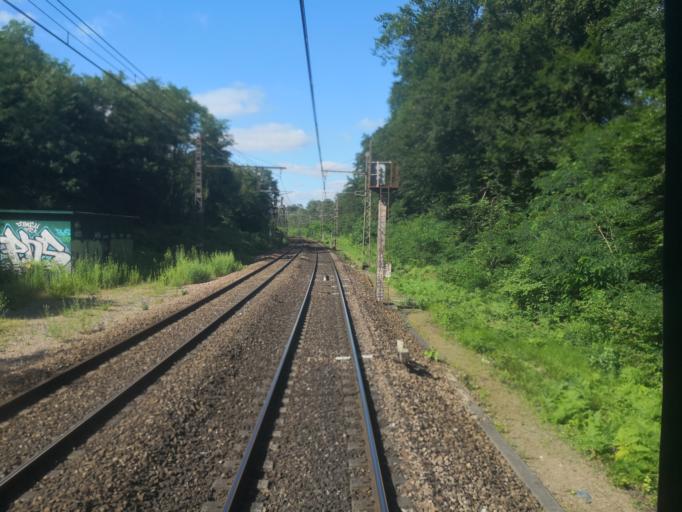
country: FR
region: Ile-de-France
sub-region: Departement de Seine-et-Marne
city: Samoreau
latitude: 48.4252
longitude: 2.7348
